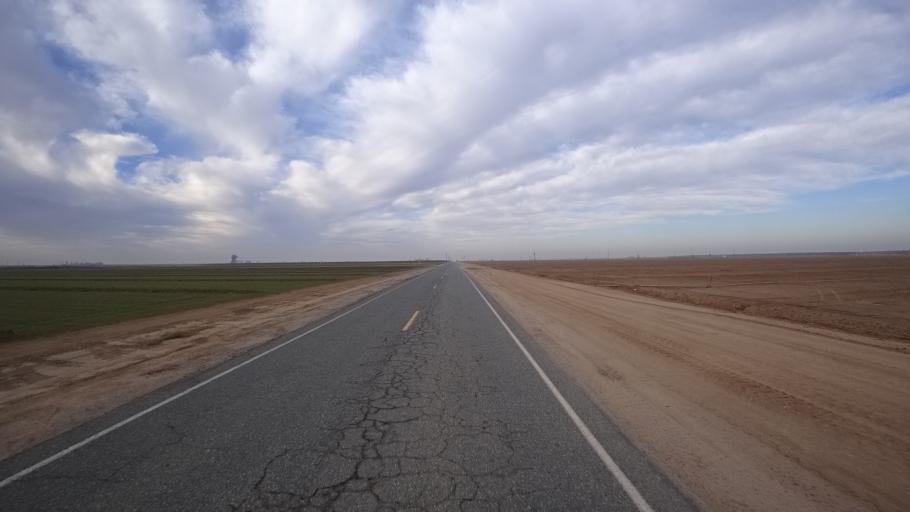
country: US
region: California
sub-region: Kern County
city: Rosedale
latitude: 35.4125
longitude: -119.1666
